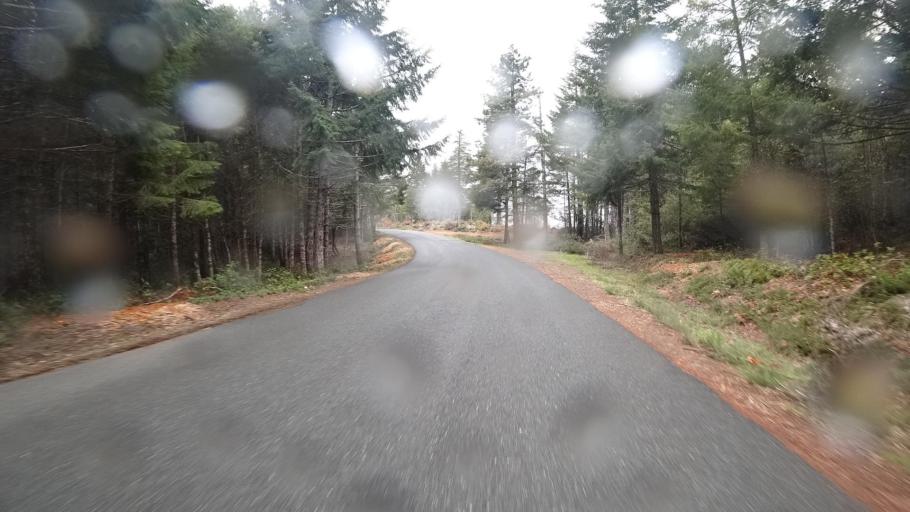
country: US
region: California
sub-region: Humboldt County
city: Willow Creek
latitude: 41.2021
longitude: -123.8006
